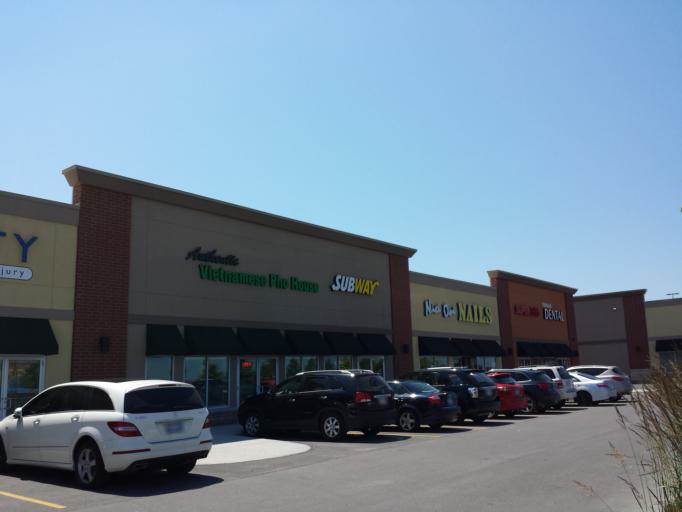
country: CA
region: Ontario
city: Bells Corners
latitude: 45.2740
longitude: -75.8708
